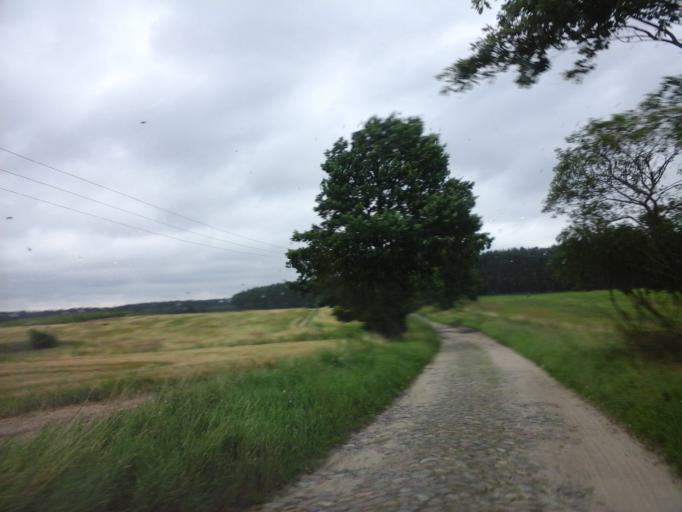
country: PL
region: West Pomeranian Voivodeship
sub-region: Powiat choszczenski
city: Pelczyce
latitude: 52.9768
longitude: 15.3448
